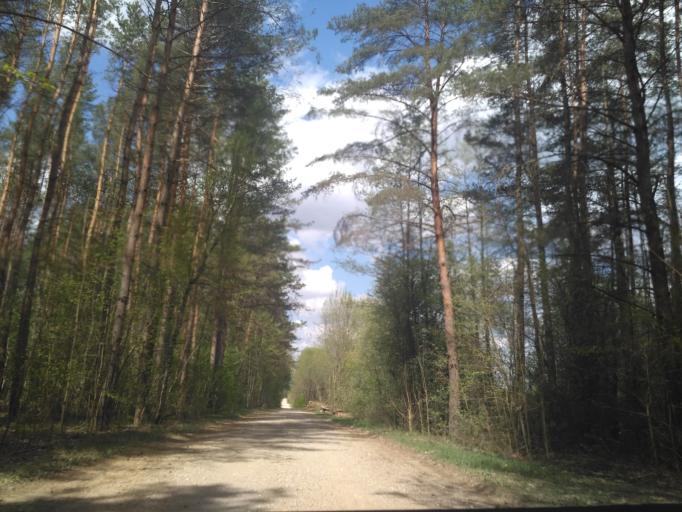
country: BY
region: Minsk
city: Il'ya
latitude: 54.2855
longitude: 27.2953
